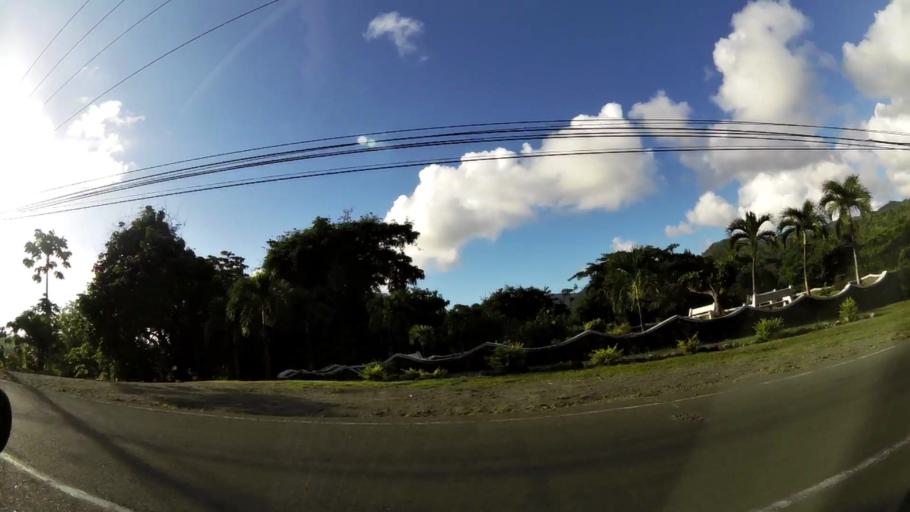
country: TT
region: Eastern Tobago
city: Roxborough
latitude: 11.2256
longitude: -60.6127
